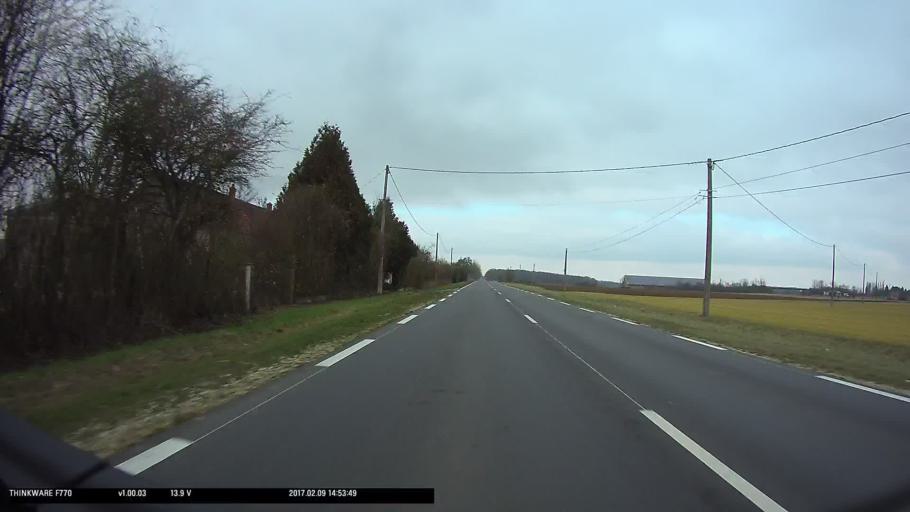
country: FR
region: Centre
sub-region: Departement du Cher
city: Levet
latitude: 46.9013
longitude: 2.4136
